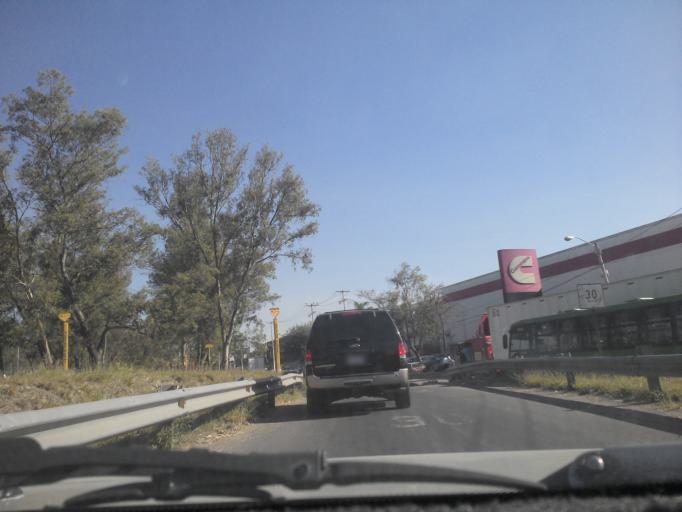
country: MX
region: Jalisco
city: Guadalajara
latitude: 20.6535
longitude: -103.4452
